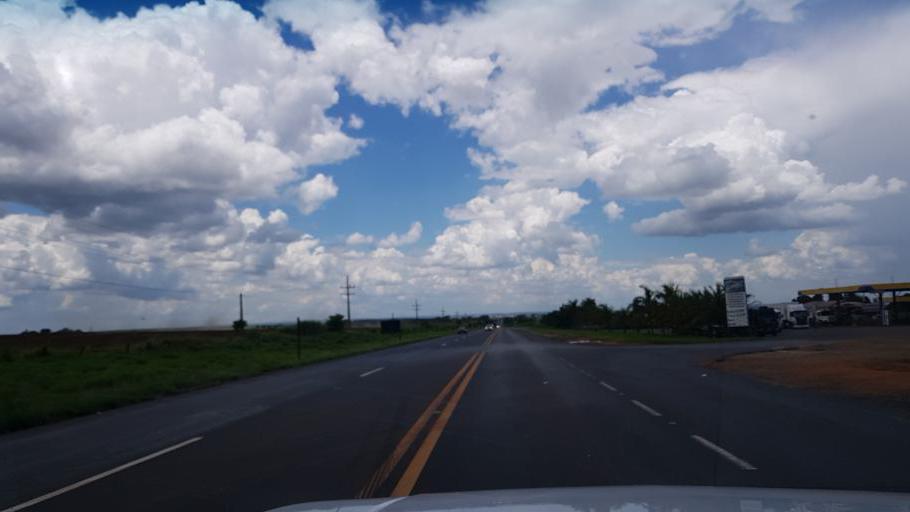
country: BR
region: Sao Paulo
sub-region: Paraguacu Paulista
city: Paraguacu Paulista
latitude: -22.3699
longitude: -50.6263
